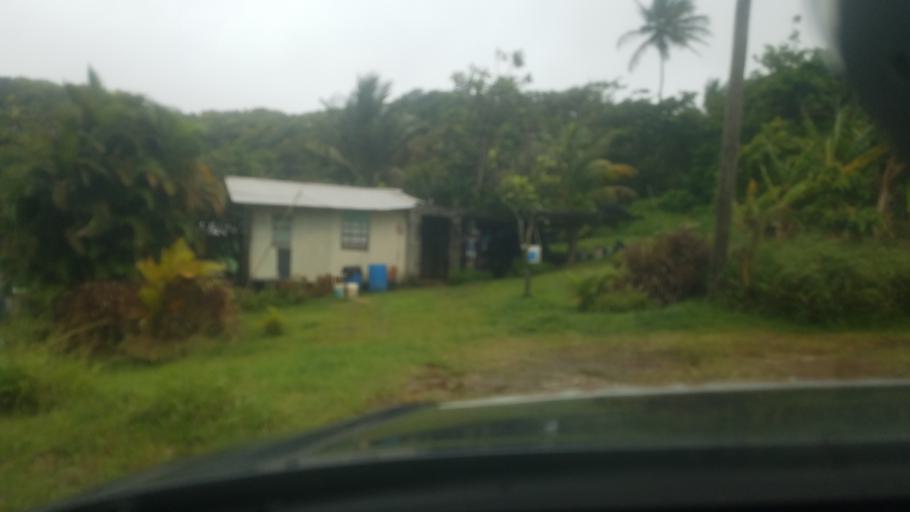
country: LC
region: Gros-Islet
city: Gros Islet
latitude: 14.0334
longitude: -60.9323
